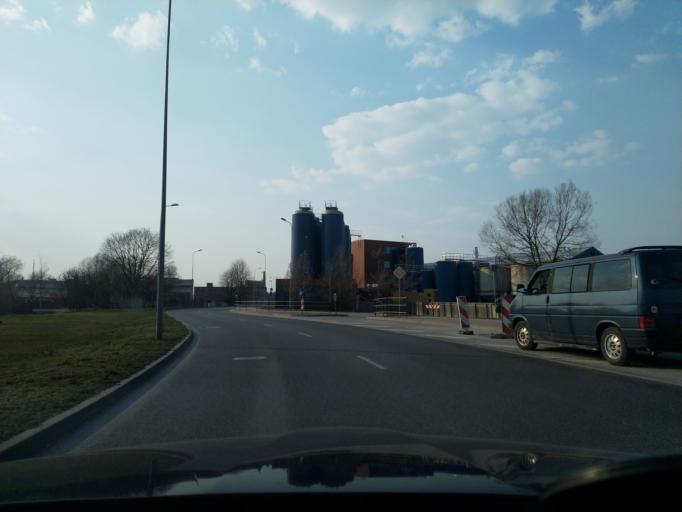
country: LV
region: Liepaja
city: Liepaja
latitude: 56.5096
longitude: 21.0254
